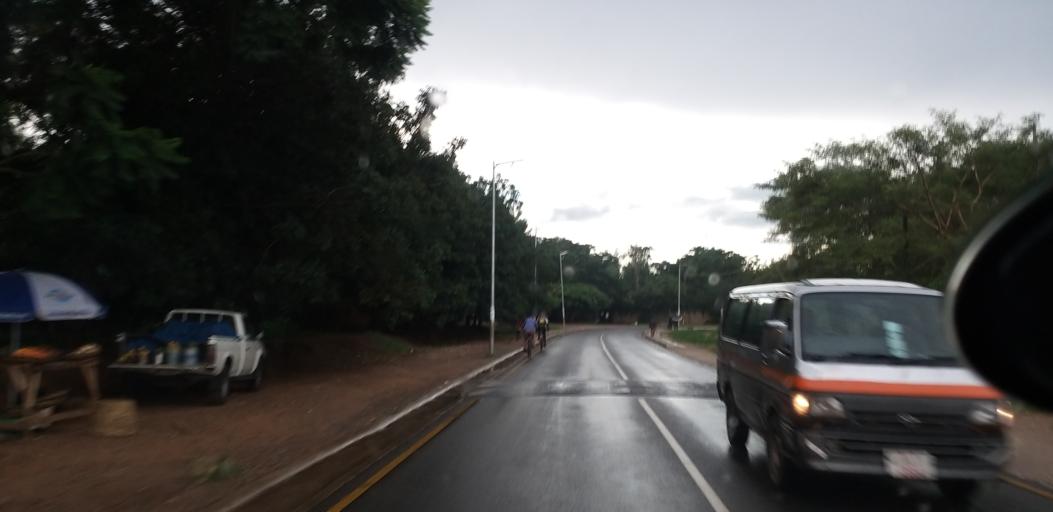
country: ZM
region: Lusaka
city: Lusaka
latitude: -15.4189
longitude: 28.3576
